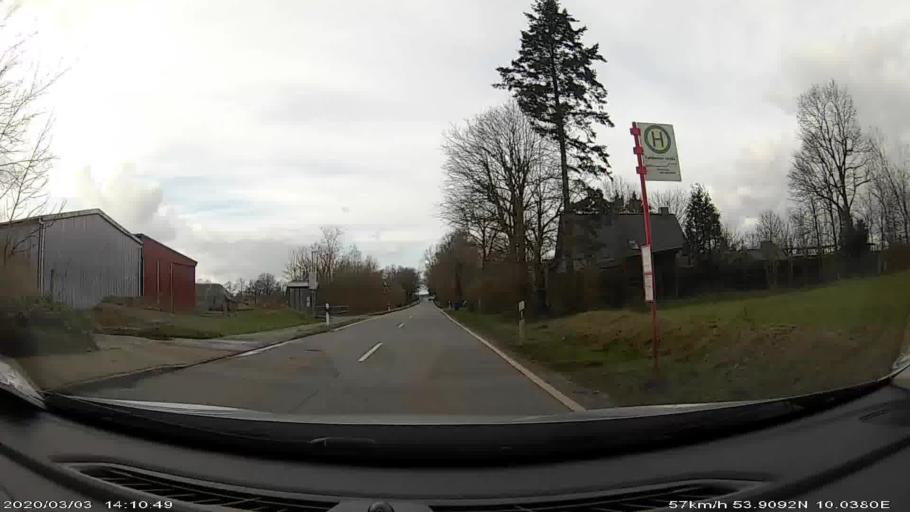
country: DE
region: Schleswig-Holstein
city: Struvenhutten
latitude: 53.9094
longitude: 10.0373
